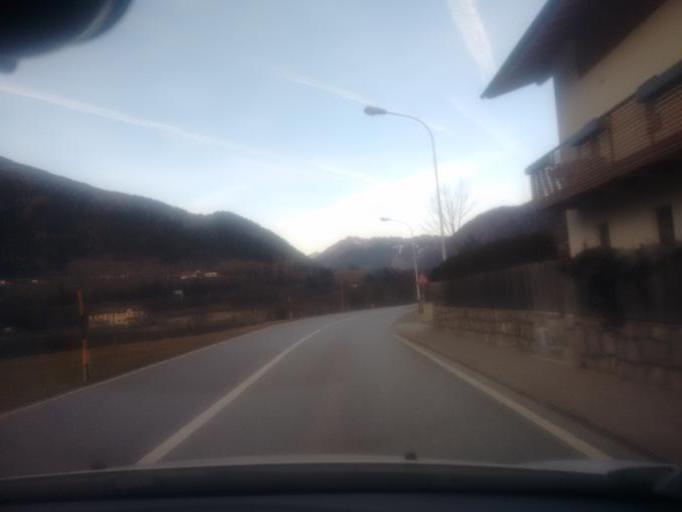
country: IT
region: Trentino-Alto Adige
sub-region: Bolzano
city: Campo di Trens
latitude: 46.8518
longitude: 11.5189
